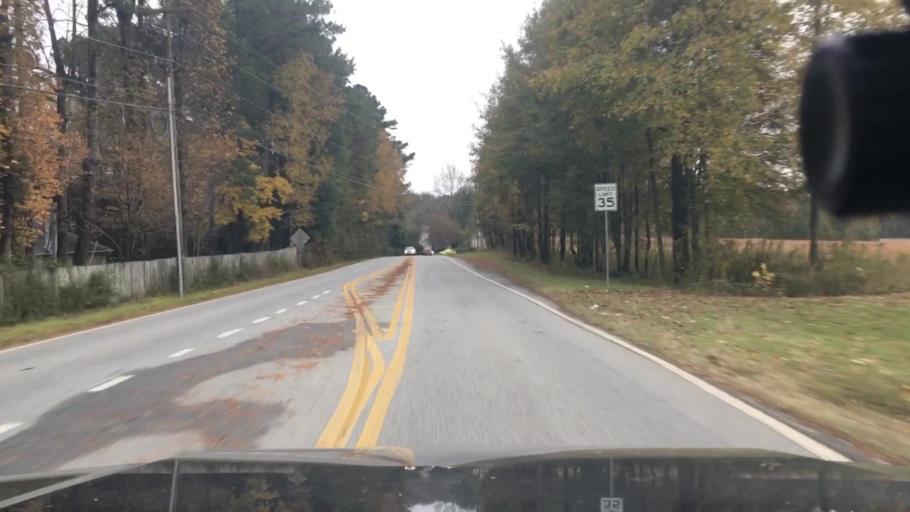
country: US
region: Georgia
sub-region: Coweta County
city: East Newnan
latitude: 33.4016
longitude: -84.7085
